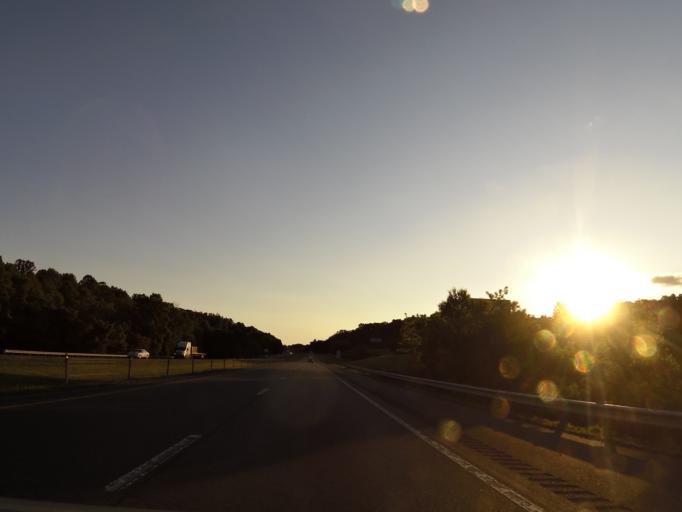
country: US
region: Tennessee
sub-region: Sullivan County
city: Colonial Heights
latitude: 36.4439
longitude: -82.5446
